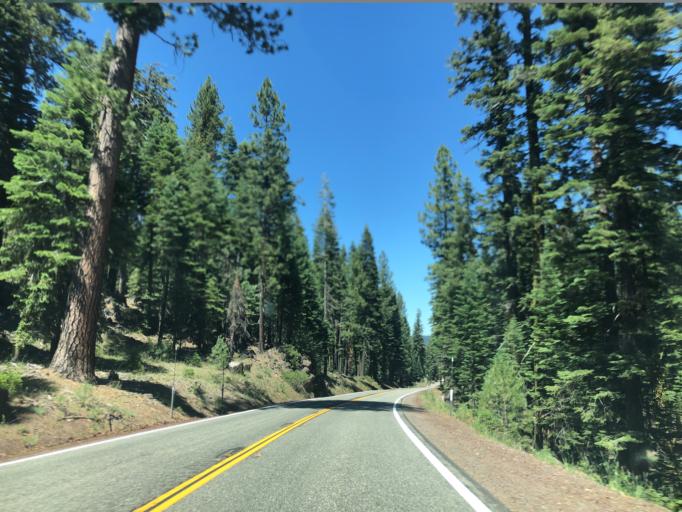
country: US
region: California
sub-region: Shasta County
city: Burney
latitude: 40.5956
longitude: -121.5358
